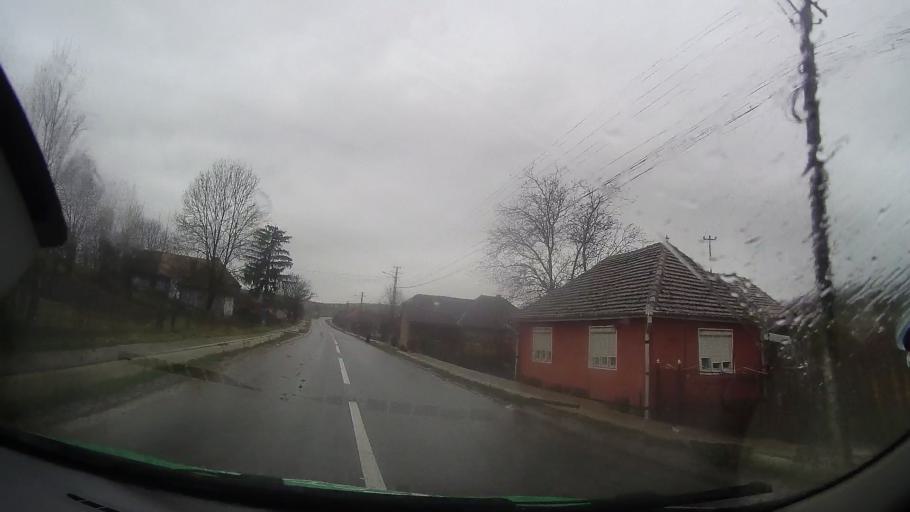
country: RO
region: Bistrita-Nasaud
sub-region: Comuna Monor
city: Monor
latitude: 46.9518
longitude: 24.6843
